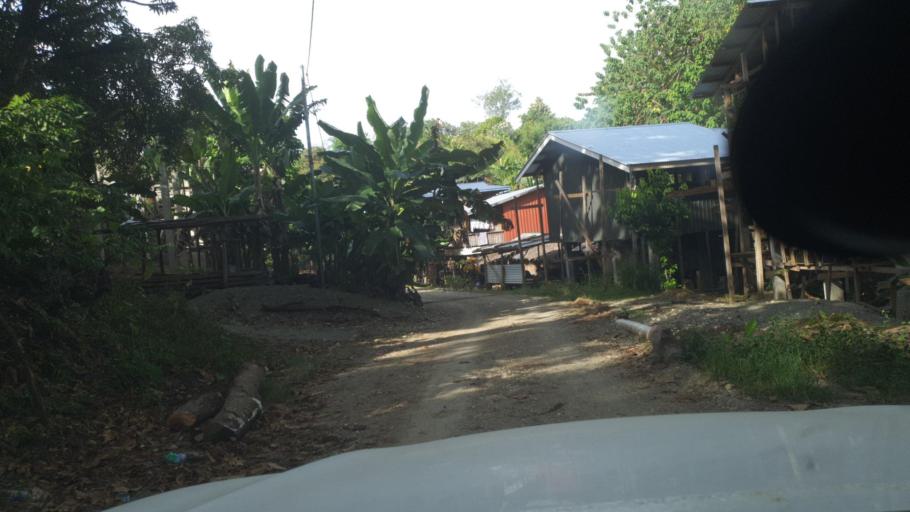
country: SB
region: Guadalcanal
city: Honiara
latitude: -9.4381
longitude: 159.9438
